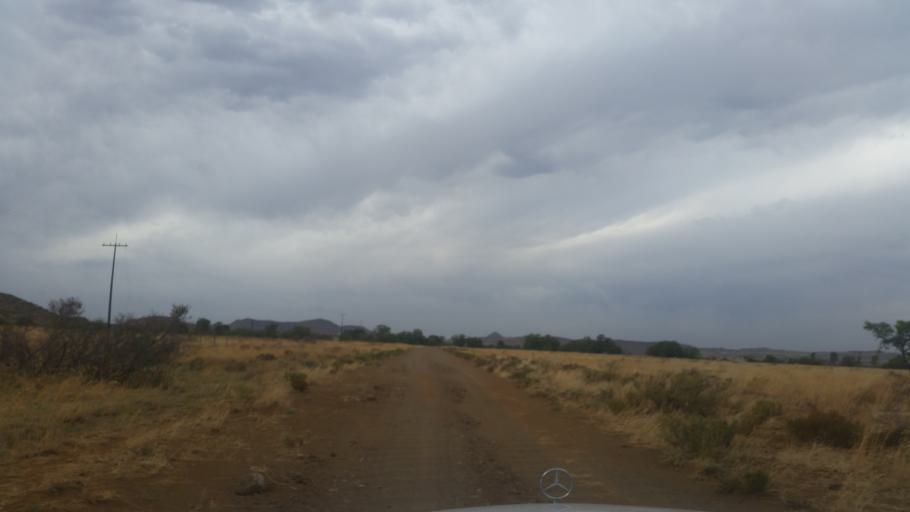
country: ZA
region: Orange Free State
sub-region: Xhariep District Municipality
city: Trompsburg
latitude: -30.5014
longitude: 25.9542
